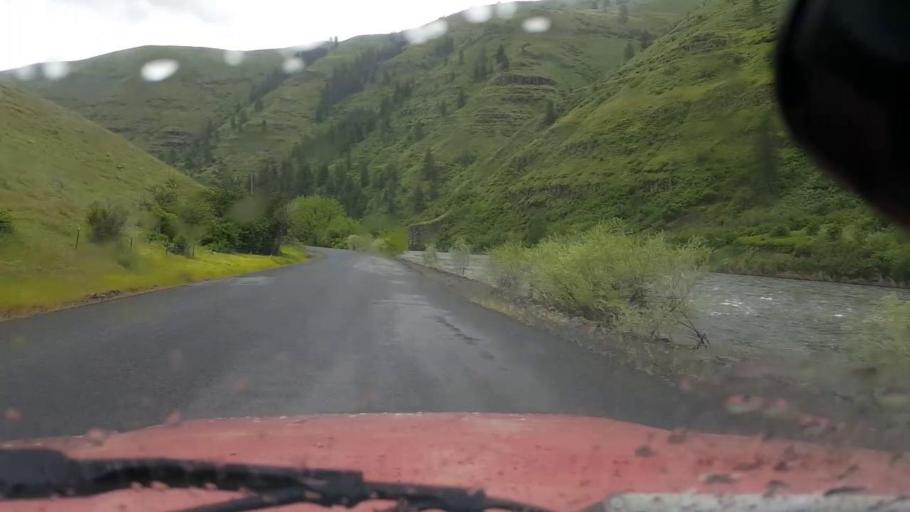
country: US
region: Washington
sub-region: Asotin County
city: Asotin
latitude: 46.0365
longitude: -117.2794
